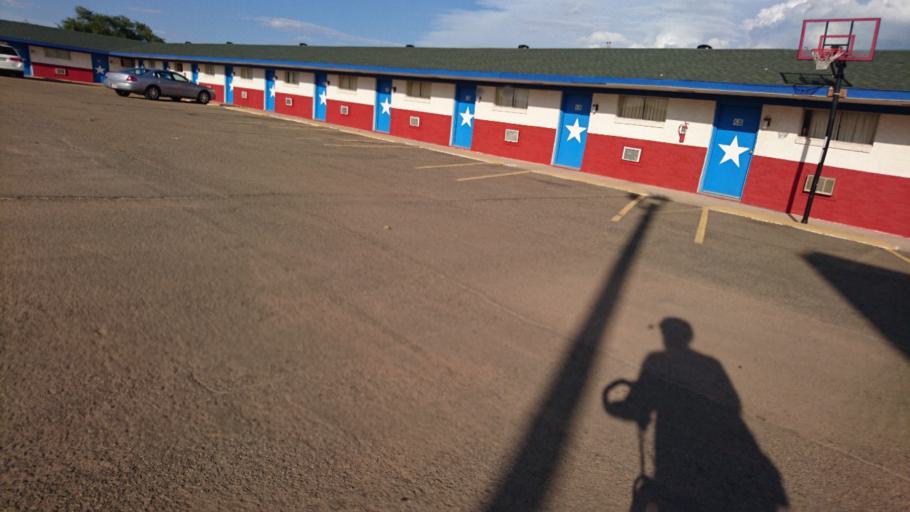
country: US
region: Texas
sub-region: Wheeler County
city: Shamrock
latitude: 35.2266
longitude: -100.2418
